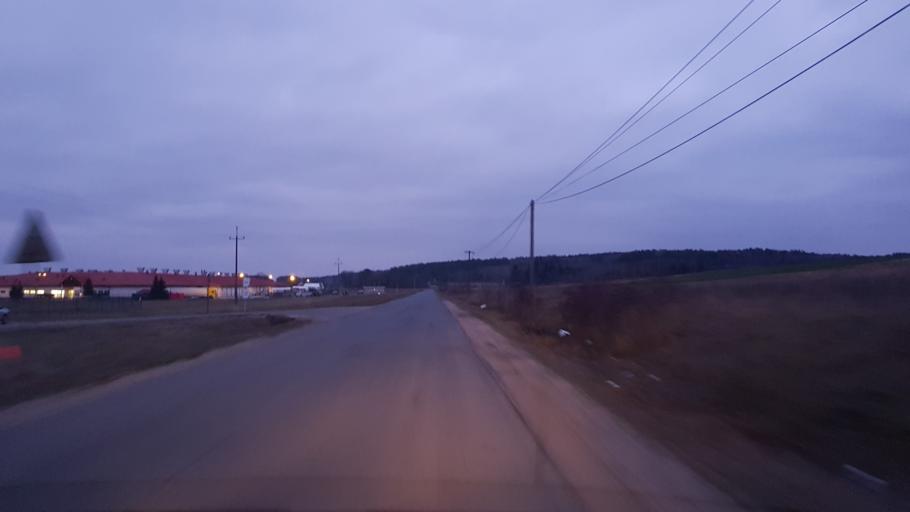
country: PL
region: Greater Poland Voivodeship
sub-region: Powiat zlotowski
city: Okonek
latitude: 53.5003
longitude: 16.8046
